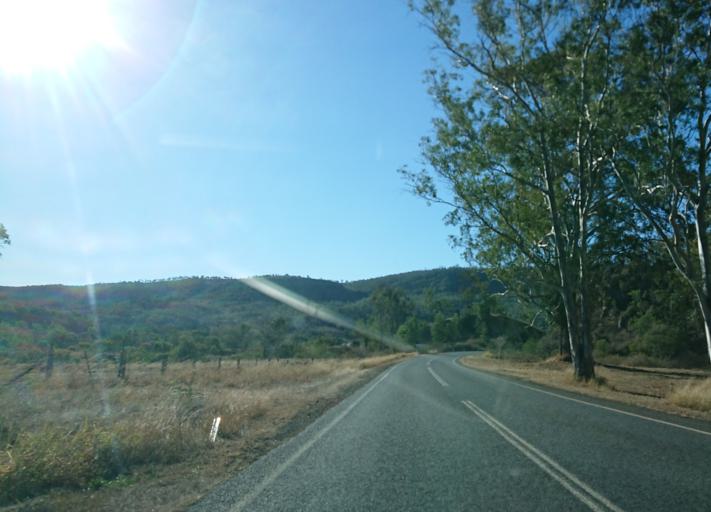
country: AU
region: Queensland
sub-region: Toowoomba
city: Rangeville
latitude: -27.7235
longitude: 152.1167
